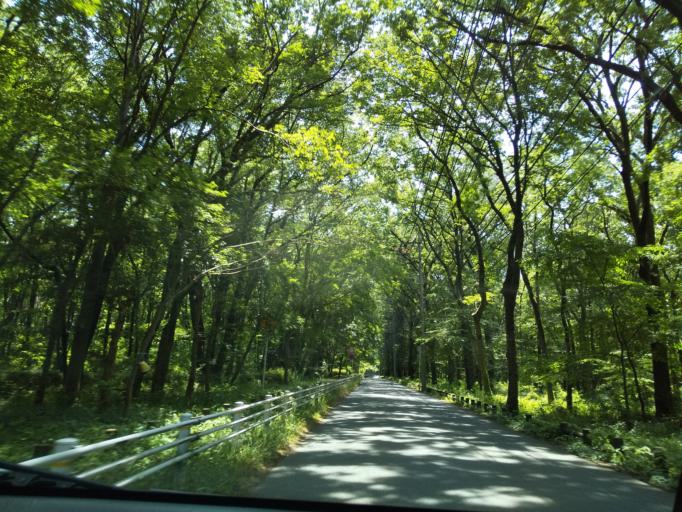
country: JP
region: Tokyo
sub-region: Machida-shi
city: Machida
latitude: 35.5449
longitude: 139.4085
